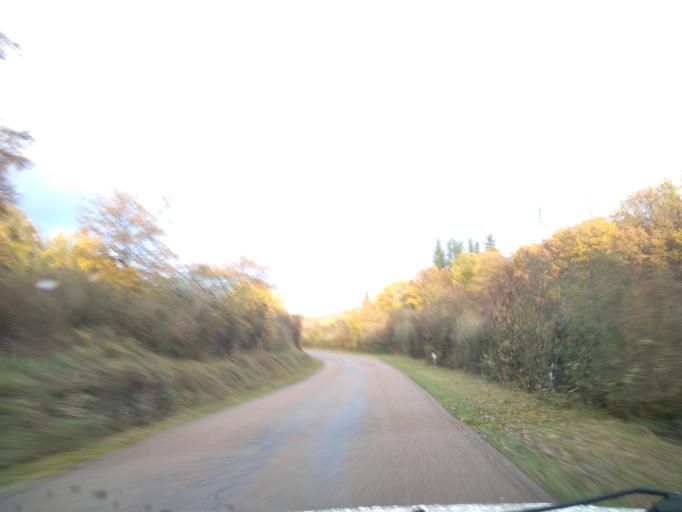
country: FR
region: Bourgogne
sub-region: Departement de Saone-et-Loire
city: Rully
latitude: 46.8839
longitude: 4.7169
